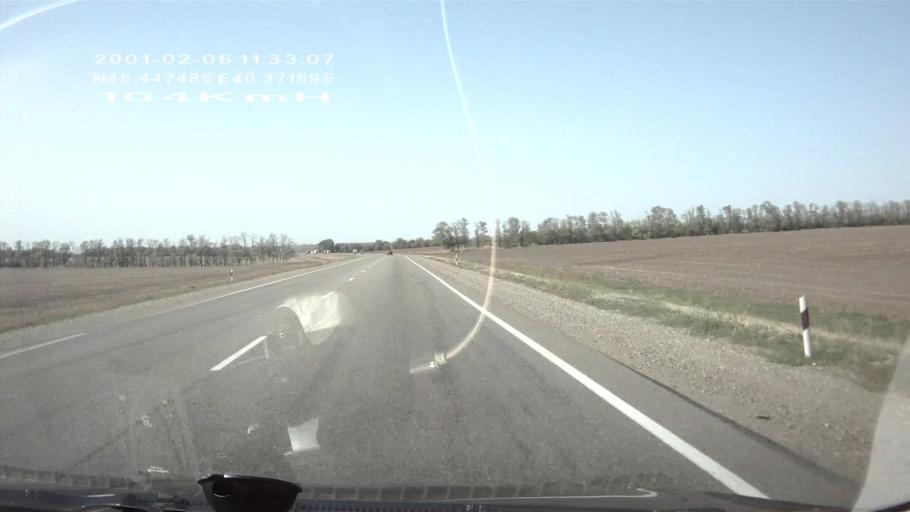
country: RU
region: Krasnodarskiy
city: Kazanskaya
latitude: 45.4472
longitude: 40.3707
